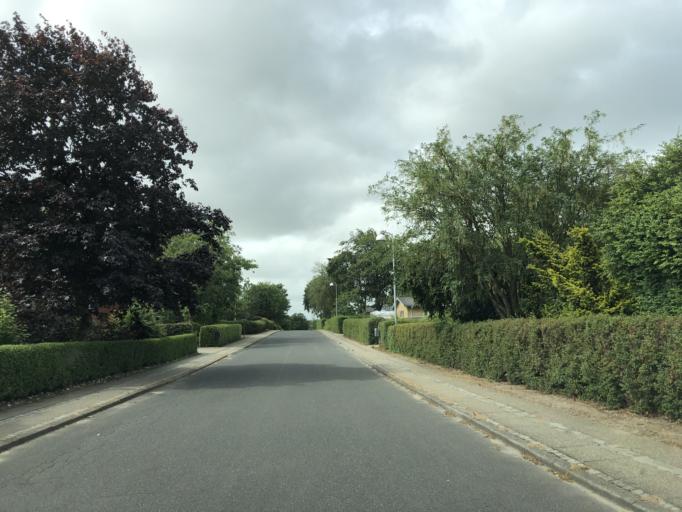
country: DK
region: Central Jutland
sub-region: Ringkobing-Skjern Kommune
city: Videbaek
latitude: 56.1992
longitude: 8.5709
